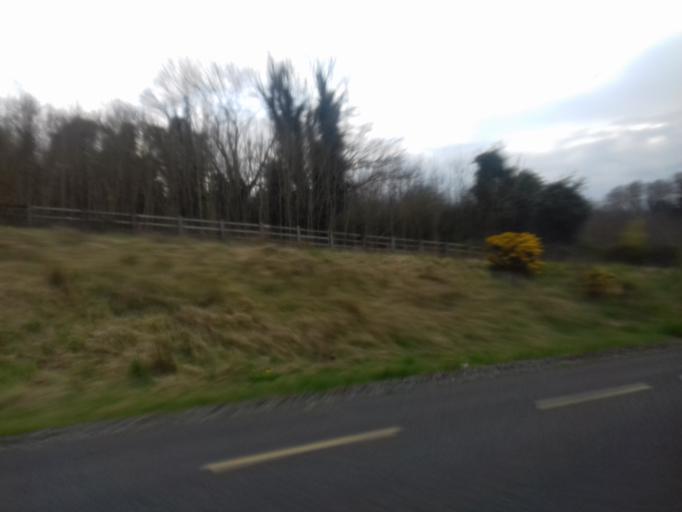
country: IE
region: Ulster
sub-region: An Cabhan
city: Belturbet
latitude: 54.0845
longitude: -7.4396
